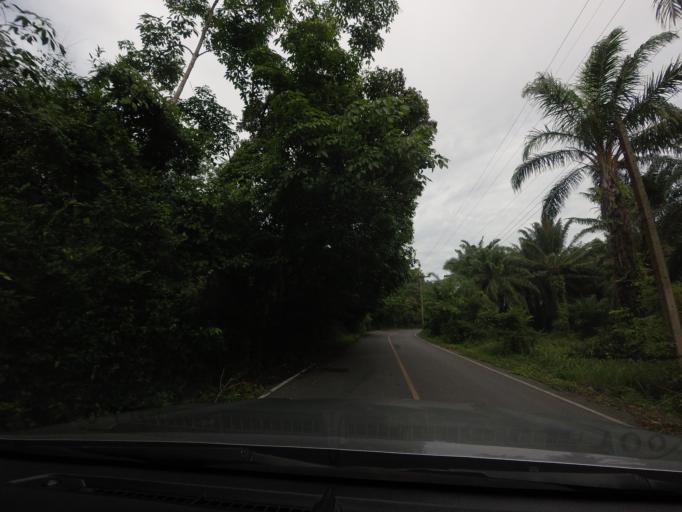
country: TH
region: Nakhon Si Thammarat
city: Phra Phrom
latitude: 8.2810
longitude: 99.9394
